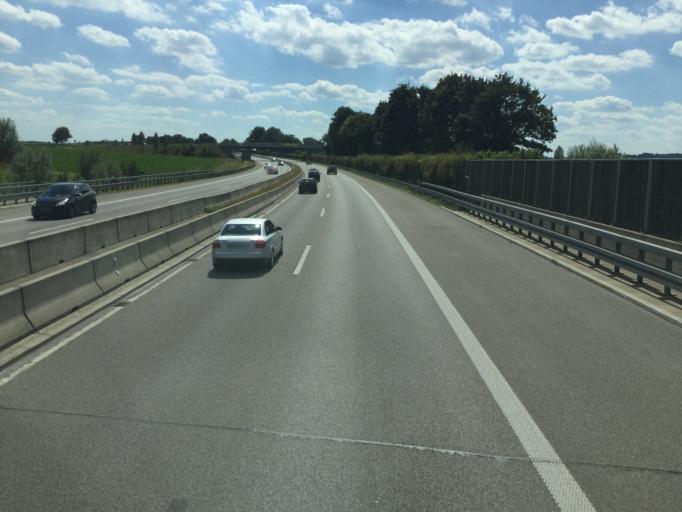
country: DE
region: Bavaria
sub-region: Swabia
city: Holzgunz
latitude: 48.0186
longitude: 10.2623
